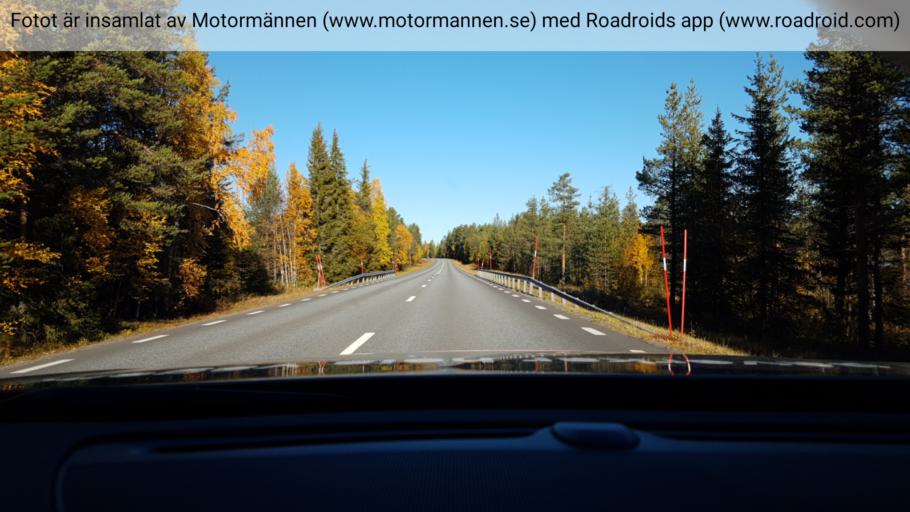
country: SE
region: Norrbotten
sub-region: Arvidsjaurs Kommun
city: Arvidsjaur
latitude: 65.5104
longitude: 19.2827
